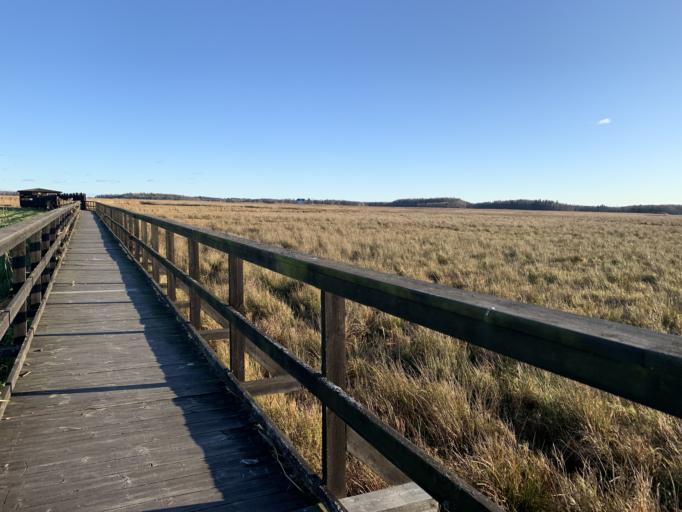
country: SE
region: Soedermanland
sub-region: Eskilstuna Kommun
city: Torshalla
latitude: 59.5218
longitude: 16.4519
